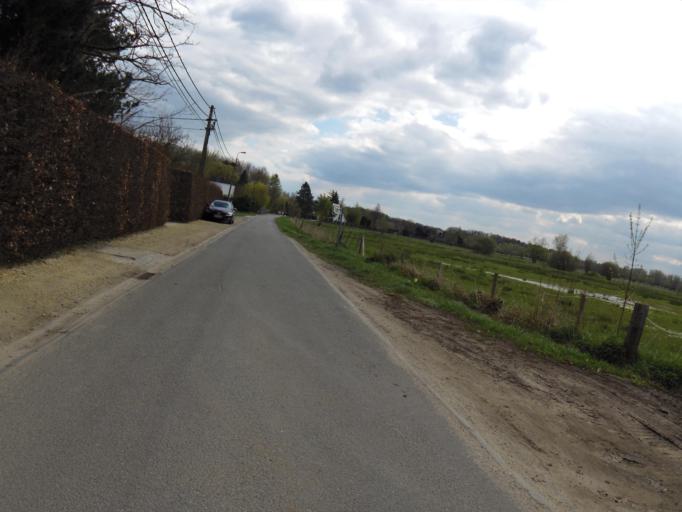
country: BE
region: Flanders
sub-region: Provincie Oost-Vlaanderen
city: Sint-Martens-Latem
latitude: 51.0329
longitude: 3.6206
